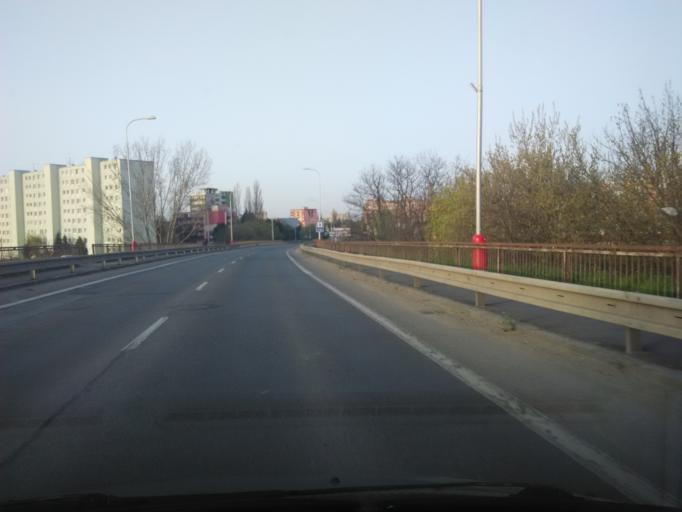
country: SK
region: Nitriansky
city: Sellye
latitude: 48.1591
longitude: 17.8788
